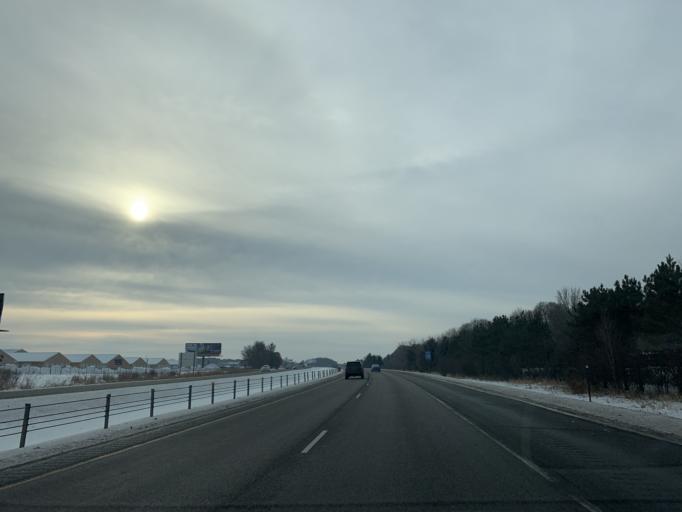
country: US
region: Minnesota
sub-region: Chisago County
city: Wyoming
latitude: 45.3312
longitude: -93.0048
